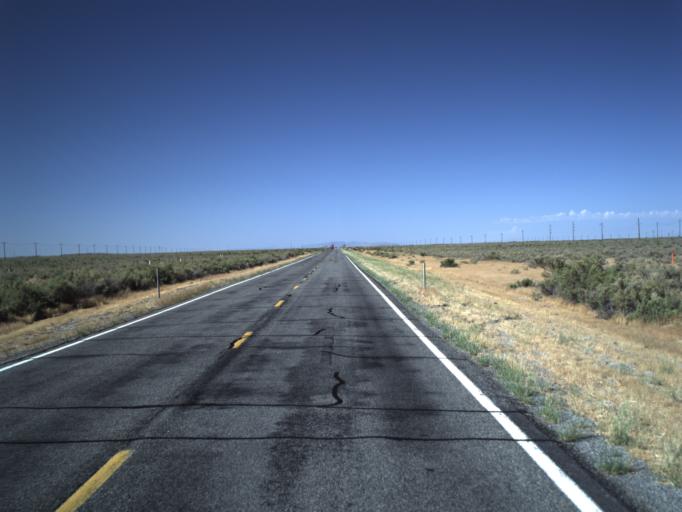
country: US
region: Utah
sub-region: Millard County
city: Delta
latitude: 39.4703
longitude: -112.4243
